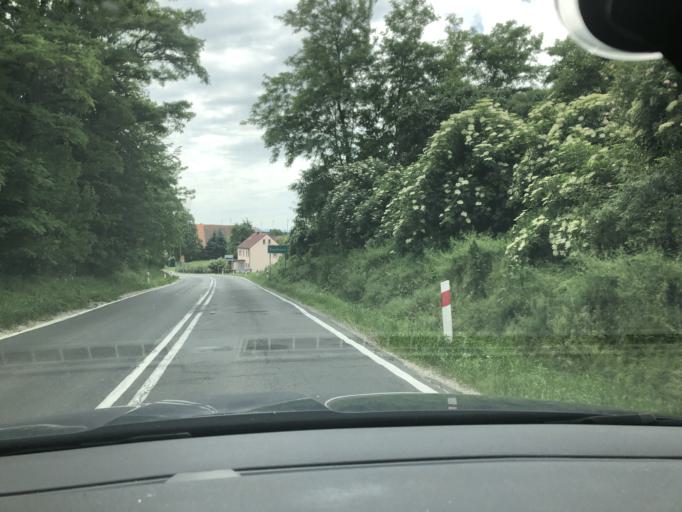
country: PL
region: Lower Silesian Voivodeship
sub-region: Powiat legnicki
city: Chojnow
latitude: 51.2120
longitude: 15.9253
